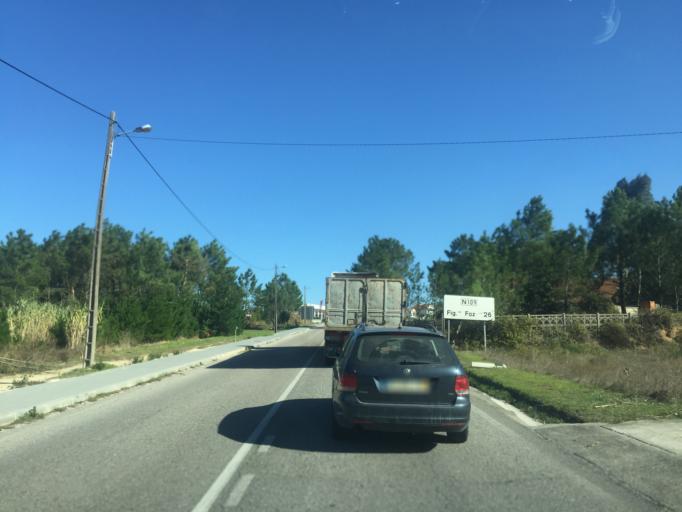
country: PT
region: Leiria
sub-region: Leiria
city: Monte Redondo
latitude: 39.9415
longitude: -8.7937
